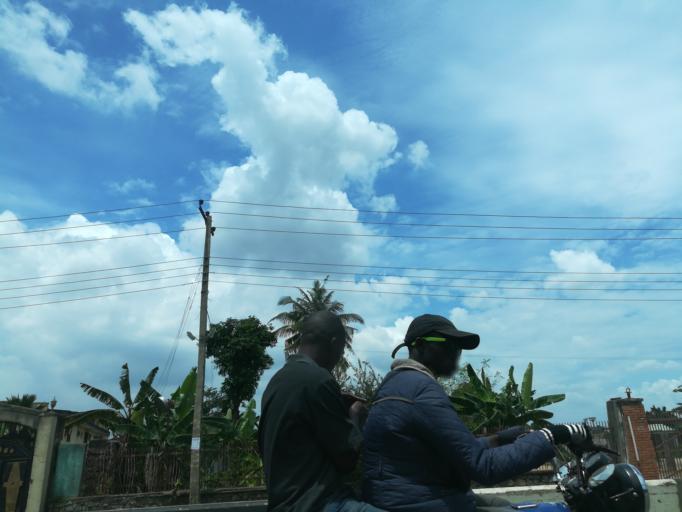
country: NG
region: Lagos
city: Ebute Ikorodu
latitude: 6.5994
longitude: 3.4950
